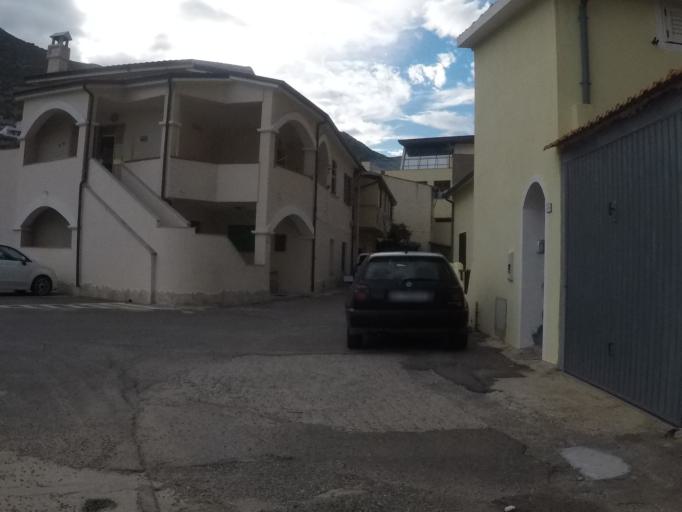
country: IT
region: Sardinia
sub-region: Provincia di Carbonia-Iglesias
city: Buggerru
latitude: 39.3998
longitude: 8.3994
